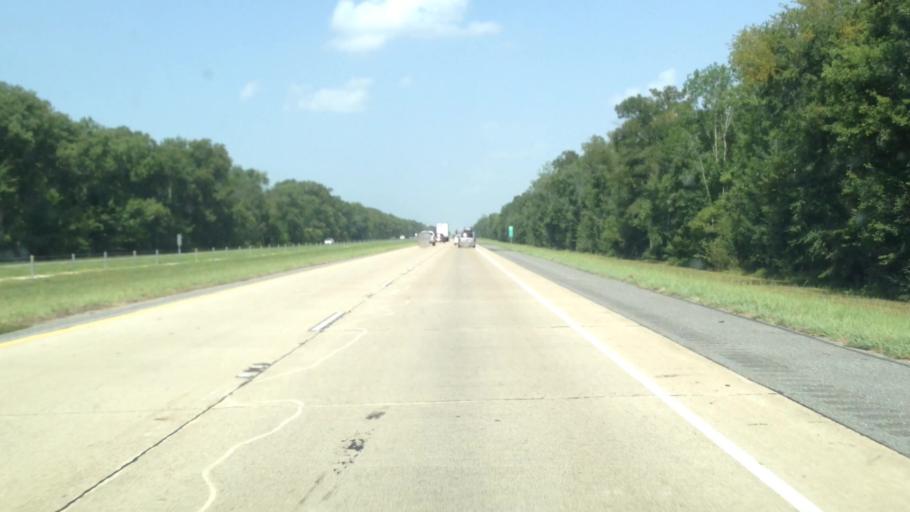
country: US
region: Louisiana
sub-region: Ouachita Parish
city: Lakeshore
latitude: 32.4865
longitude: -91.9590
